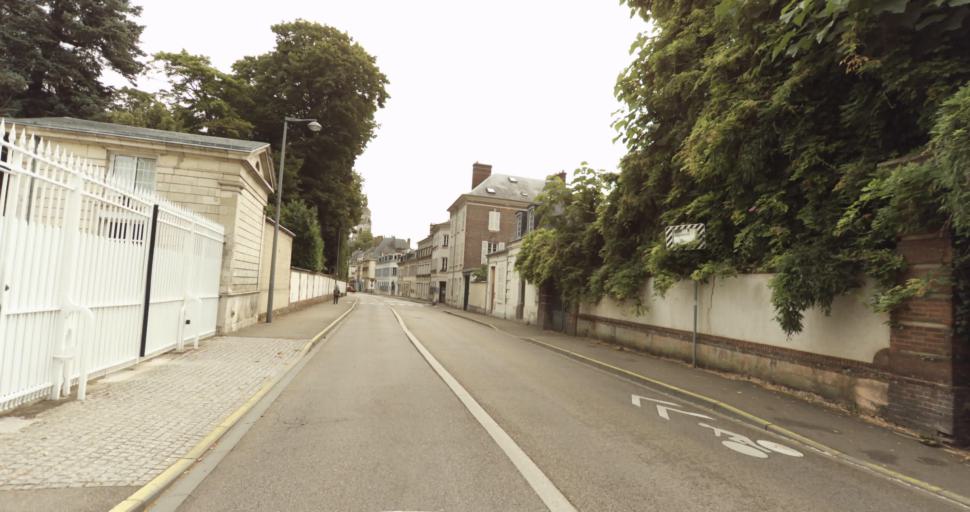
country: FR
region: Haute-Normandie
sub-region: Departement de l'Eure
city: Evreux
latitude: 49.0239
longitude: 1.1461
